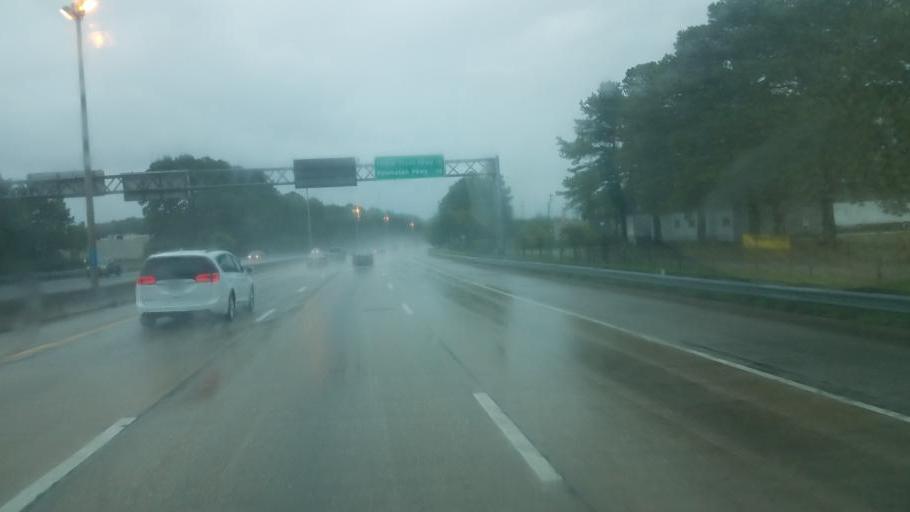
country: US
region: Virginia
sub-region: City of Newport News
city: Newport News
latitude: 37.0106
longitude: -76.3966
